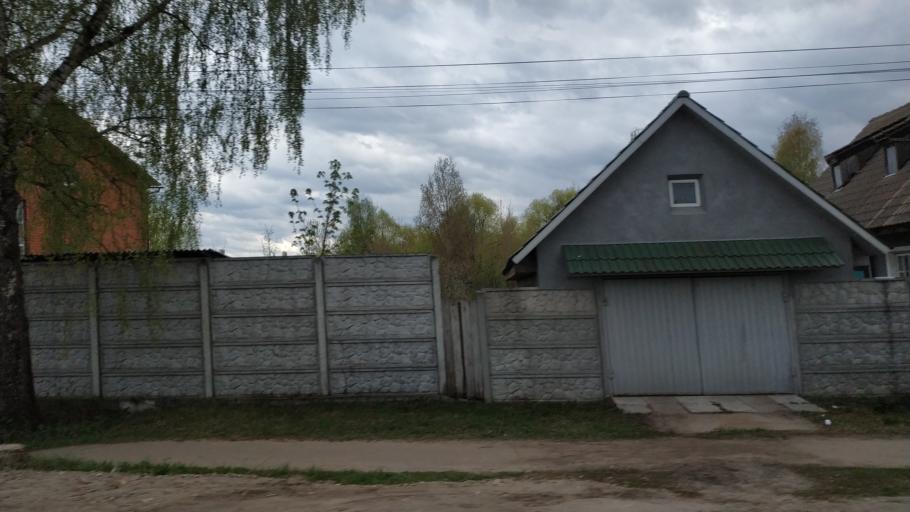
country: RU
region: Moskovskaya
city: Pavlovskiy Posad
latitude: 55.7719
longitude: 38.6905
